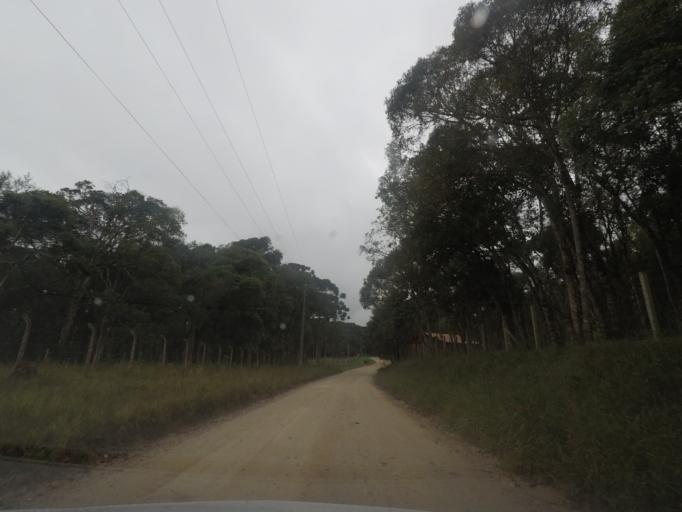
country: BR
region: Parana
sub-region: Campina Grande Do Sul
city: Campina Grande do Sul
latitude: -25.3088
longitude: -49.1005
